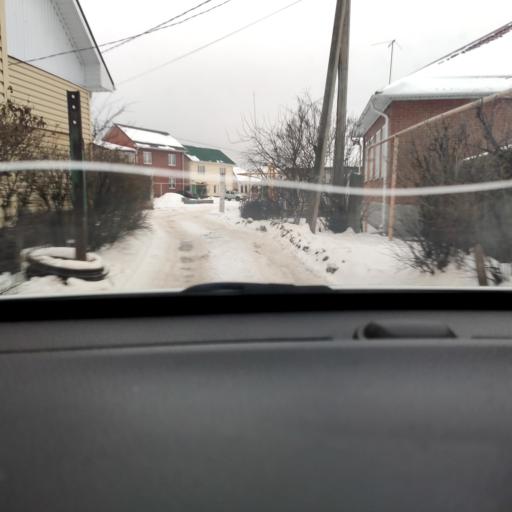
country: RU
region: Voronezj
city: Somovo
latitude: 51.7508
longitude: 39.3414
